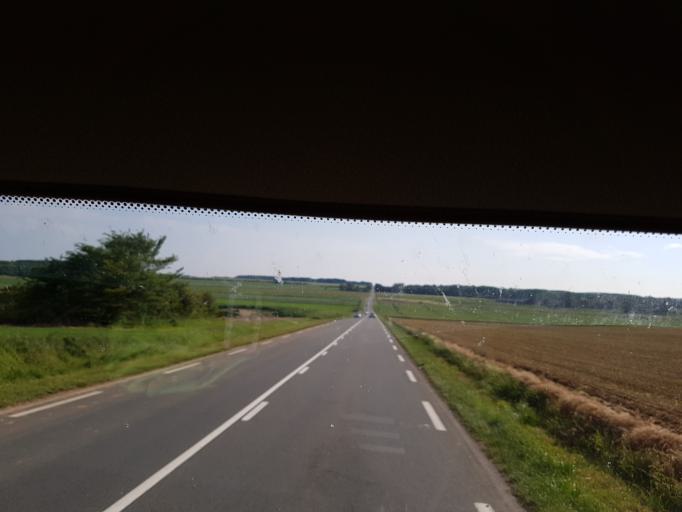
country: FR
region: Picardie
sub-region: Departement de la Somme
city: Crecy-en-Ponthieu
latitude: 50.2352
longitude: 1.9426
